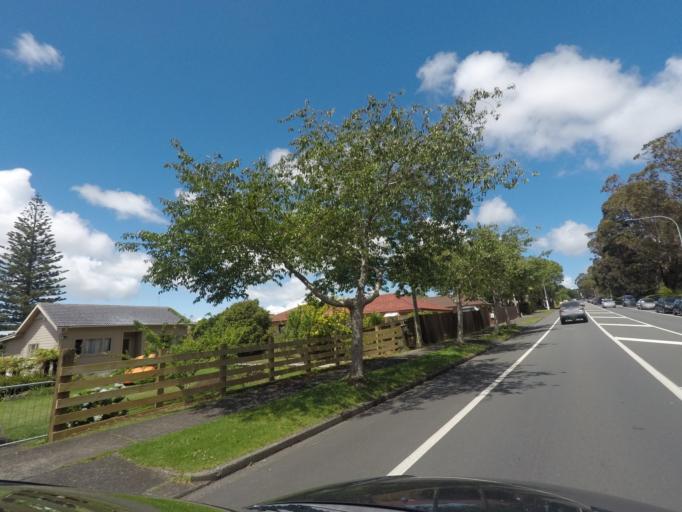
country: NZ
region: Auckland
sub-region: Auckland
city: Waitakere
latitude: -36.9040
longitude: 174.6541
